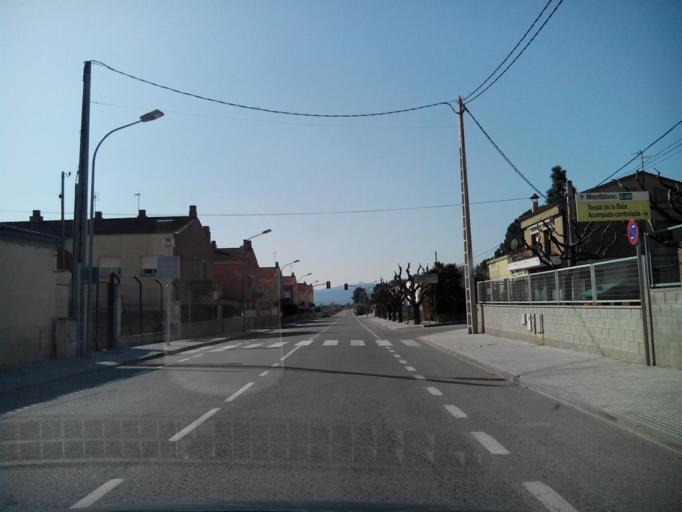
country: ES
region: Catalonia
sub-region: Provincia de Tarragona
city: Blancafort
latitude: 41.4215
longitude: 1.2008
